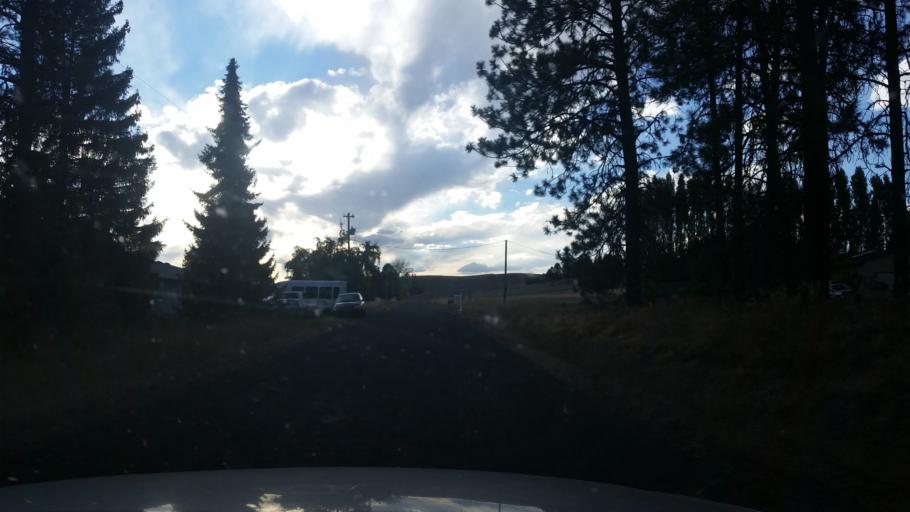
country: US
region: Washington
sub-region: Spokane County
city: Cheney
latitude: 47.4723
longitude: -117.6125
